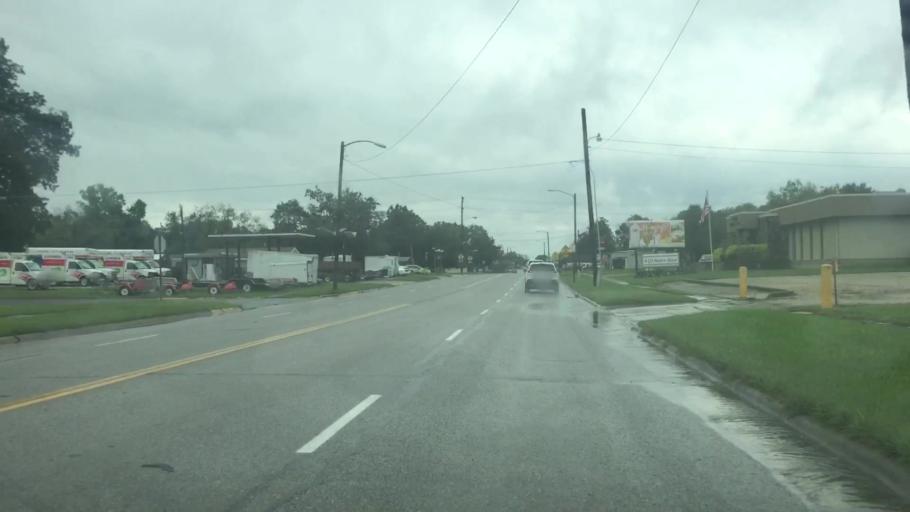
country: US
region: Kansas
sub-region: Allen County
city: Iola
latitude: 37.9270
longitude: -95.4091
